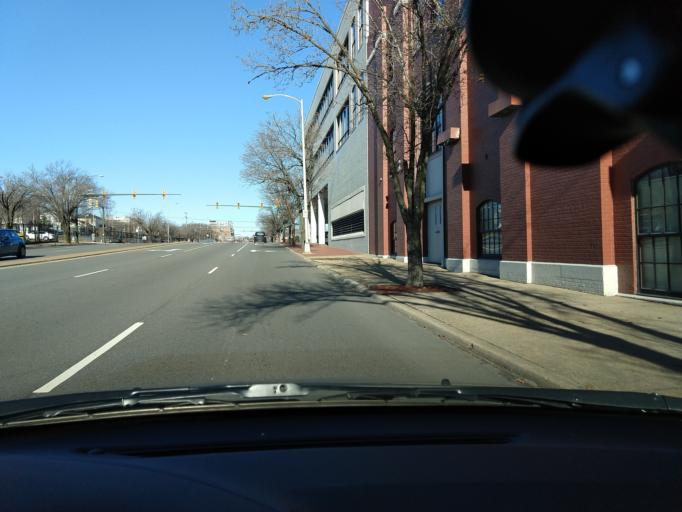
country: US
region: Virginia
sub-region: City of Richmond
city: Richmond
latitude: 37.5207
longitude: -77.4387
